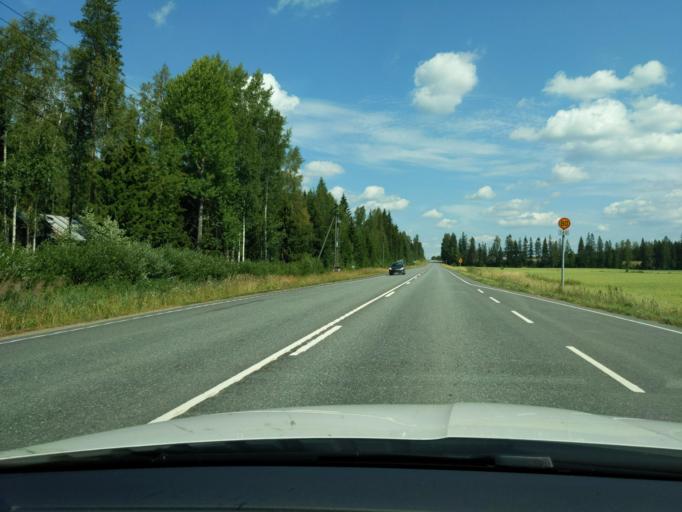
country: FI
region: Uusimaa
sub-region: Helsinki
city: Maentsaelae
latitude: 60.5560
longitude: 25.2028
